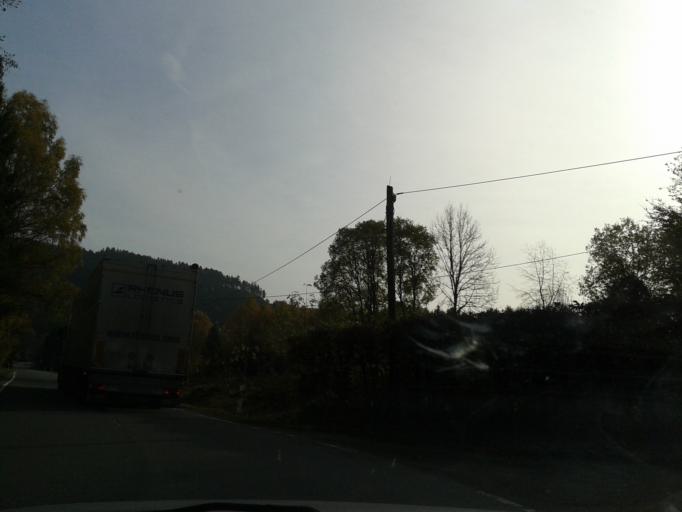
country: DE
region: North Rhine-Westphalia
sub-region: Regierungsbezirk Arnsberg
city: Bestwig
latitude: 51.3863
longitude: 8.4174
